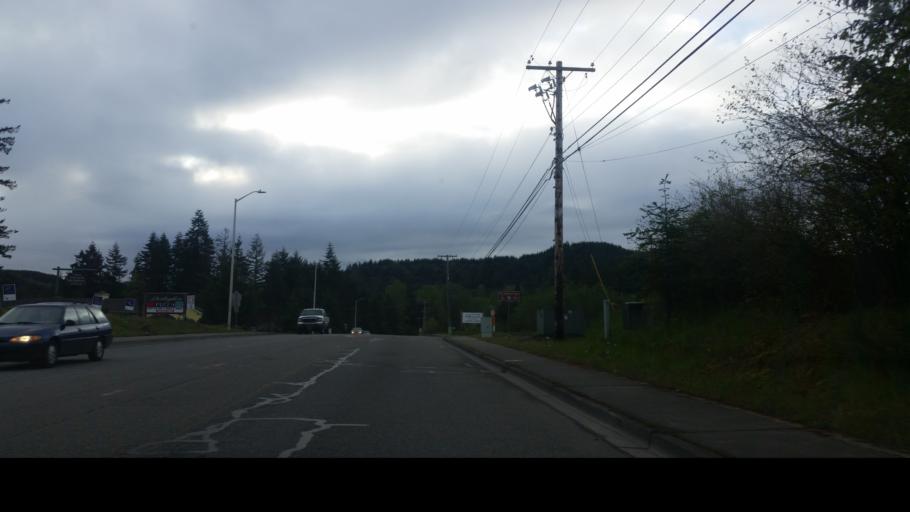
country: US
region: Washington
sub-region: Pierce County
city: Eatonville
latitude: 46.8647
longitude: -122.2582
